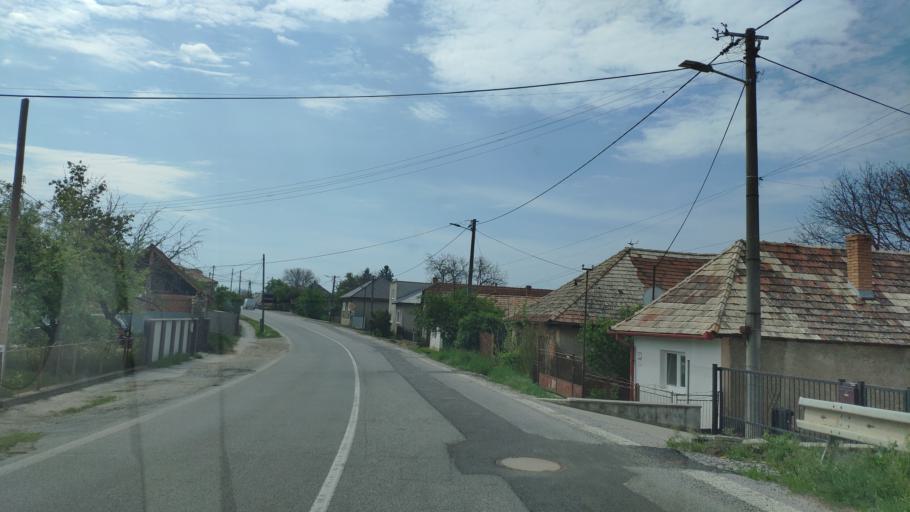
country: HU
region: Borsod-Abauj-Zemplen
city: Putnok
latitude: 48.4406
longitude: 20.3345
